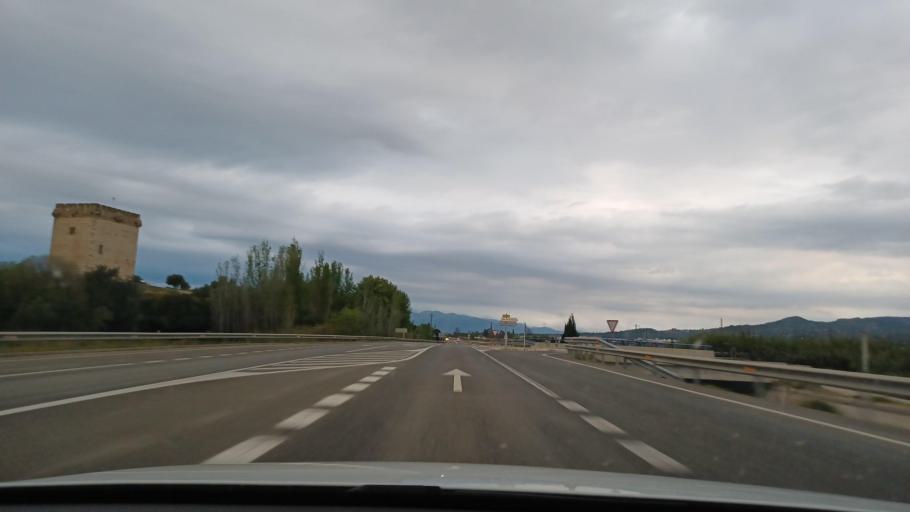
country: ES
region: Catalonia
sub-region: Provincia de Tarragona
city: Amposta
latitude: 40.7420
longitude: 0.5636
